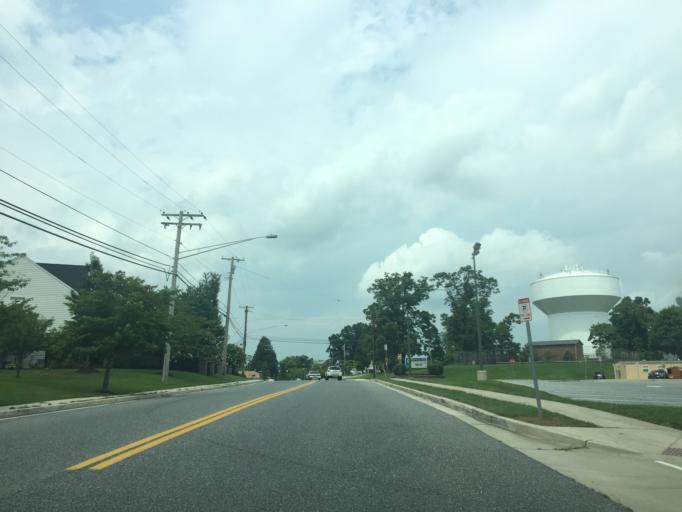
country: US
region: Maryland
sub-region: Baltimore County
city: White Marsh
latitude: 39.4002
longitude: -76.4363
